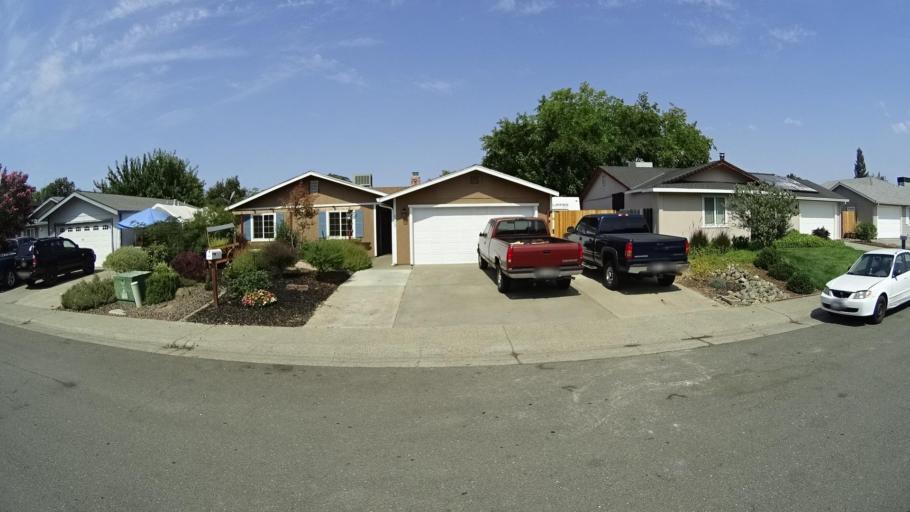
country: US
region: California
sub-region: Placer County
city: Rocklin
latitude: 38.7934
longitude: -121.2271
